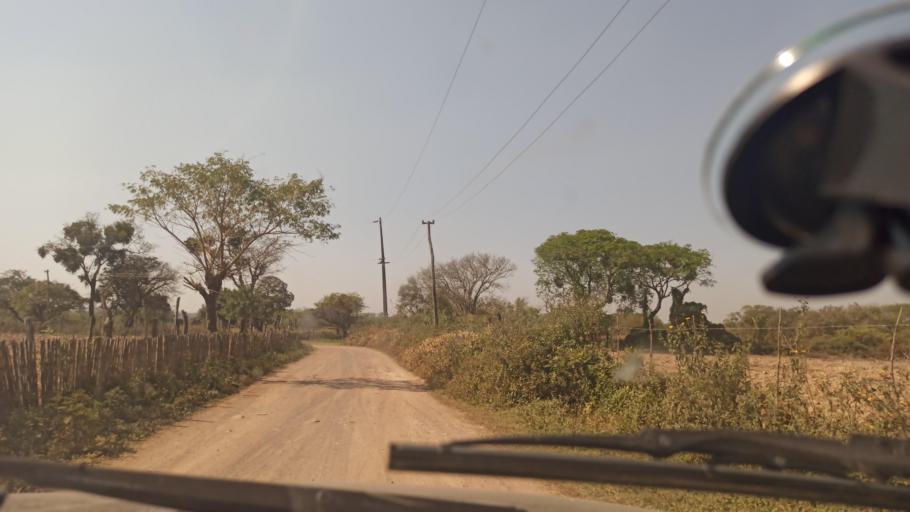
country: AR
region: Formosa
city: Clorinda
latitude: -25.3144
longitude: -57.6990
